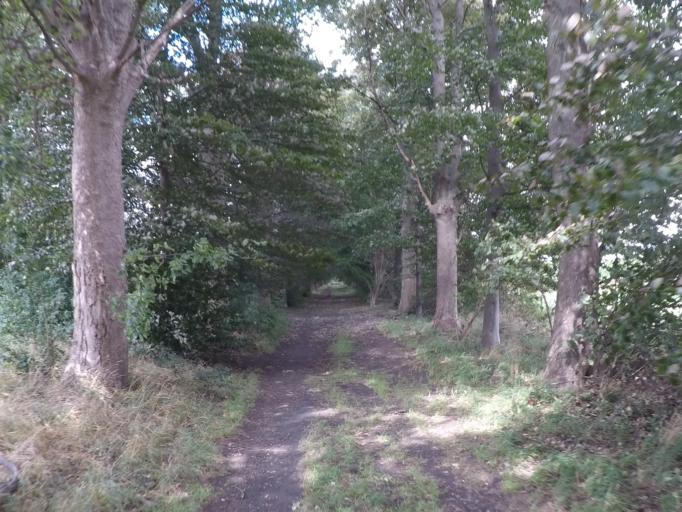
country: BE
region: Flanders
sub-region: Provincie Antwerpen
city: Ranst
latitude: 51.1863
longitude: 4.5990
